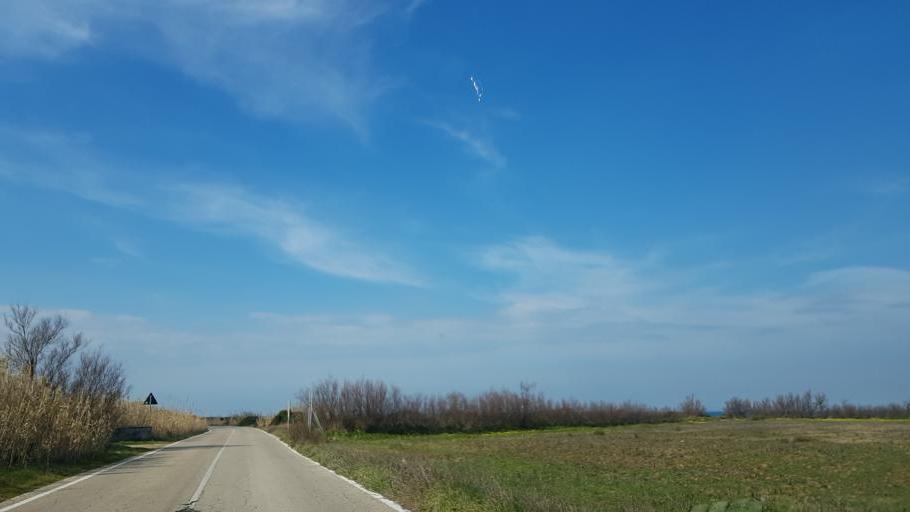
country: IT
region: Apulia
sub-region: Provincia di Brindisi
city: Brindisi
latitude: 40.6864
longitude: 17.8594
